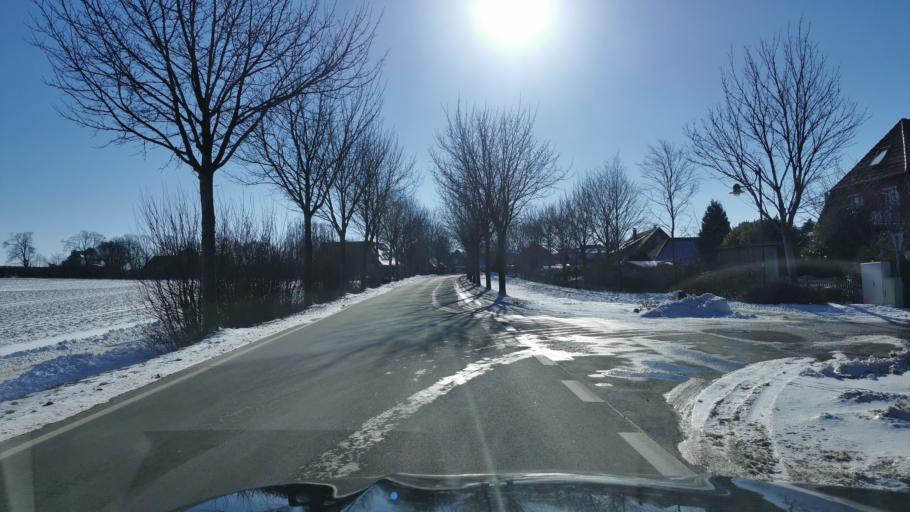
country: DE
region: Schleswig-Holstein
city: Langballig
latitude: 54.8014
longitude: 9.6378
